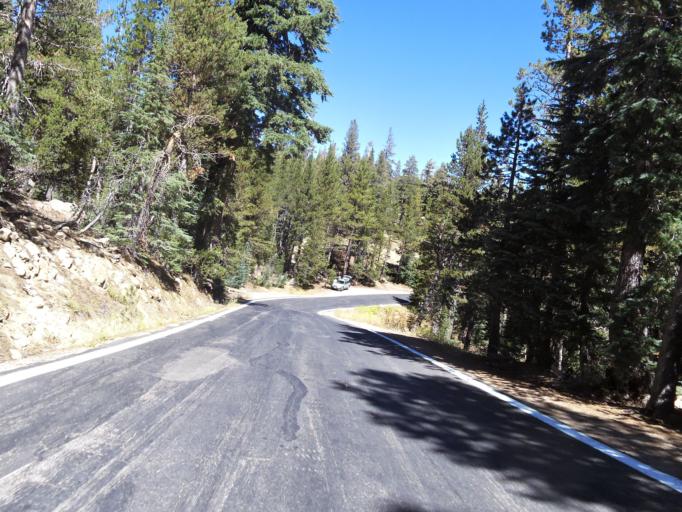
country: US
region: Nevada
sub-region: Douglas County
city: Gardnerville Ranchos
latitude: 38.5452
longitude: -119.8112
